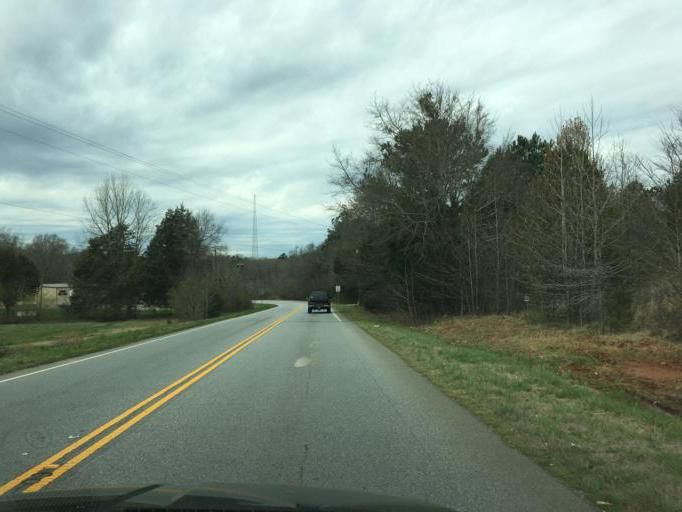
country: US
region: South Carolina
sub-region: Anderson County
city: Piedmont
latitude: 34.7070
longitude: -82.4463
